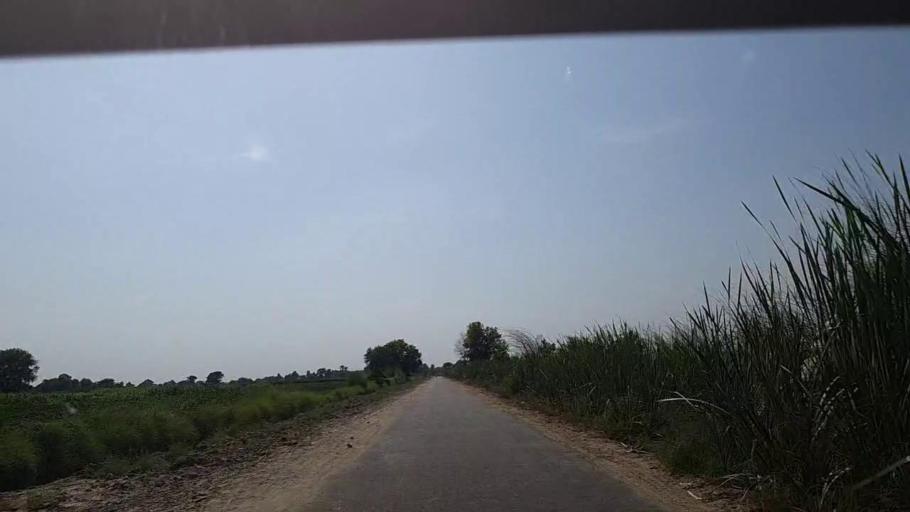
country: PK
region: Sindh
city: Khanpur
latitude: 27.8435
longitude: 69.4069
